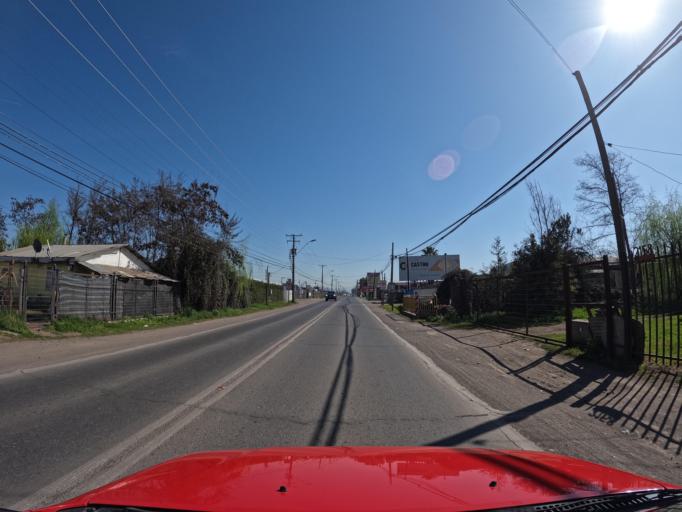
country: CL
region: Maule
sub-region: Provincia de Curico
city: Curico
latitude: -34.9631
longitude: -71.2495
